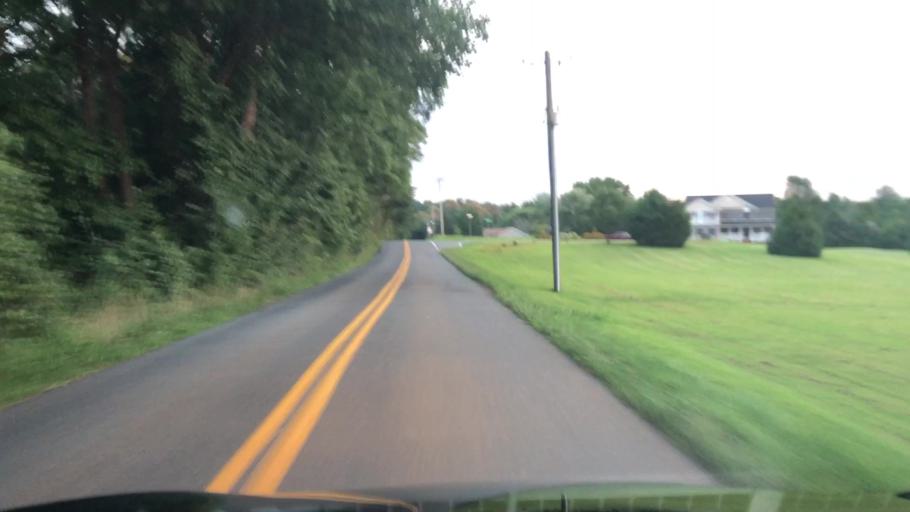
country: US
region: Virginia
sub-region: Stafford County
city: Stafford
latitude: 38.4668
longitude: -77.5788
